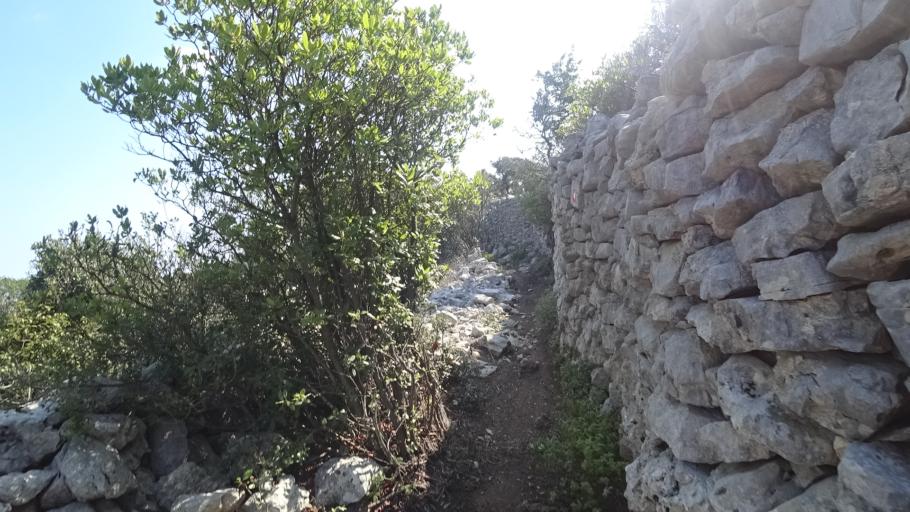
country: HR
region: Primorsko-Goranska
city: Mali Losinj
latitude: 44.4894
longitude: 14.5330
